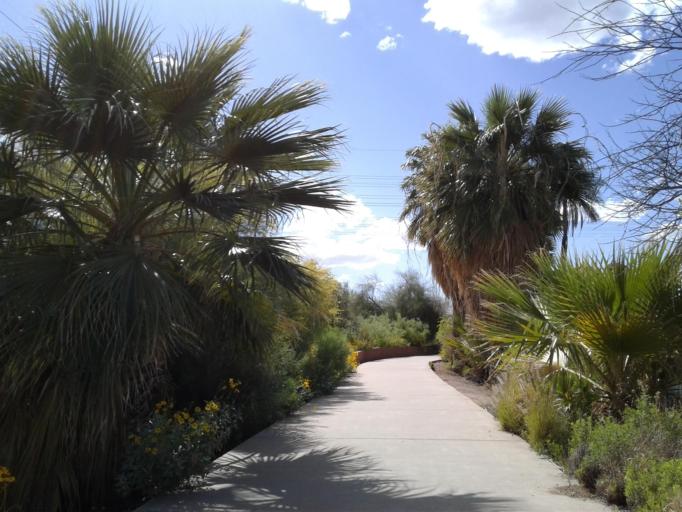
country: US
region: Arizona
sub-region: Maricopa County
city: Tempe Junction
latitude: 33.4478
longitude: -111.9384
